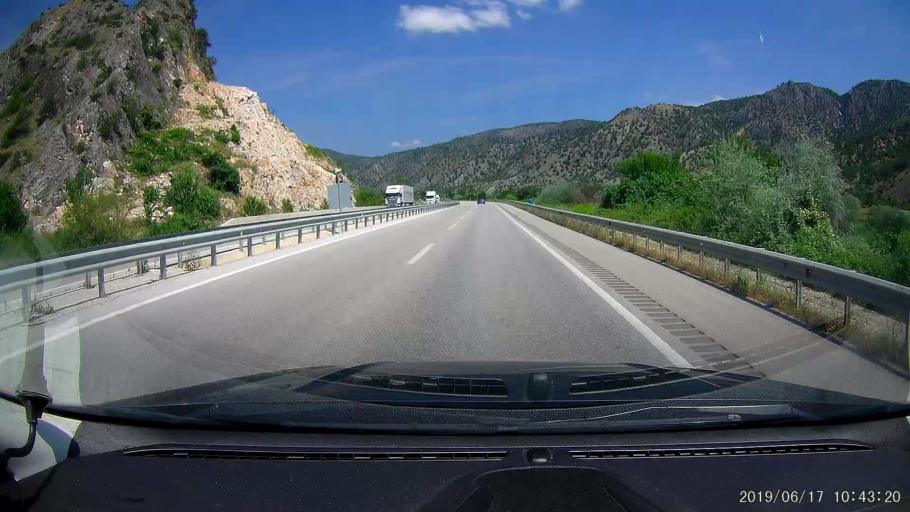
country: TR
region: Corum
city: Kargi
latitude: 41.0628
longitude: 34.5376
